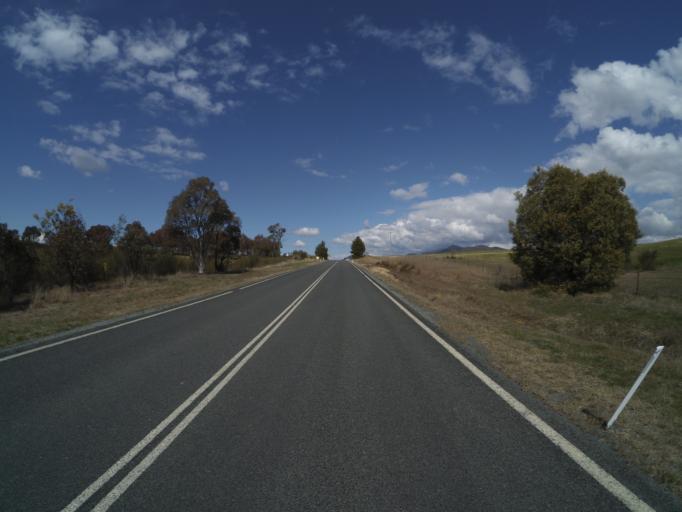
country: AU
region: Australian Capital Territory
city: Macarthur
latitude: -35.4154
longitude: 148.9461
